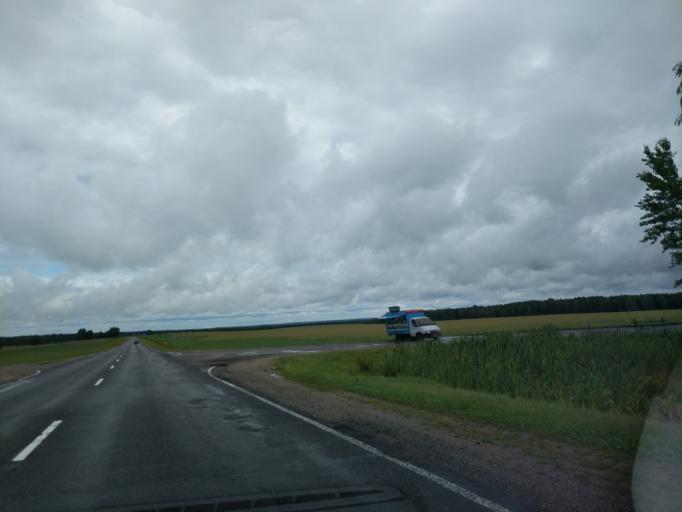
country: BY
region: Minsk
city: Il'ya
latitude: 54.3240
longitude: 27.4662
